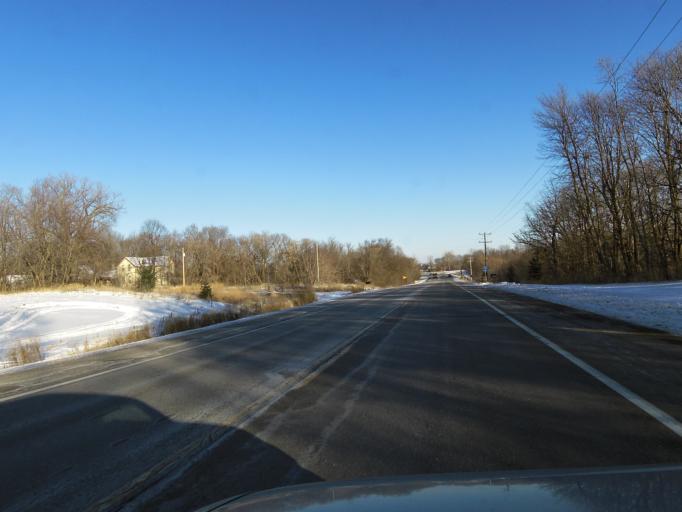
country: US
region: Minnesota
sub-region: Scott County
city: Prior Lake
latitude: 44.7237
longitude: -93.4902
